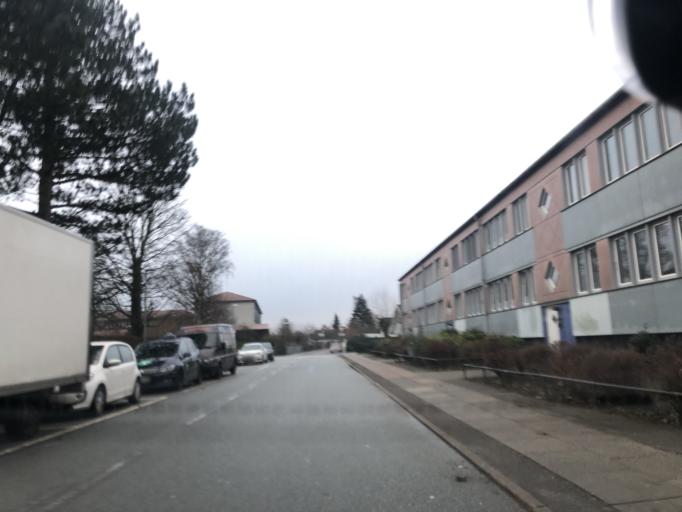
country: DK
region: Capital Region
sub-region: Tarnby Kommune
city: Tarnby
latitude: 55.6320
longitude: 12.5976
